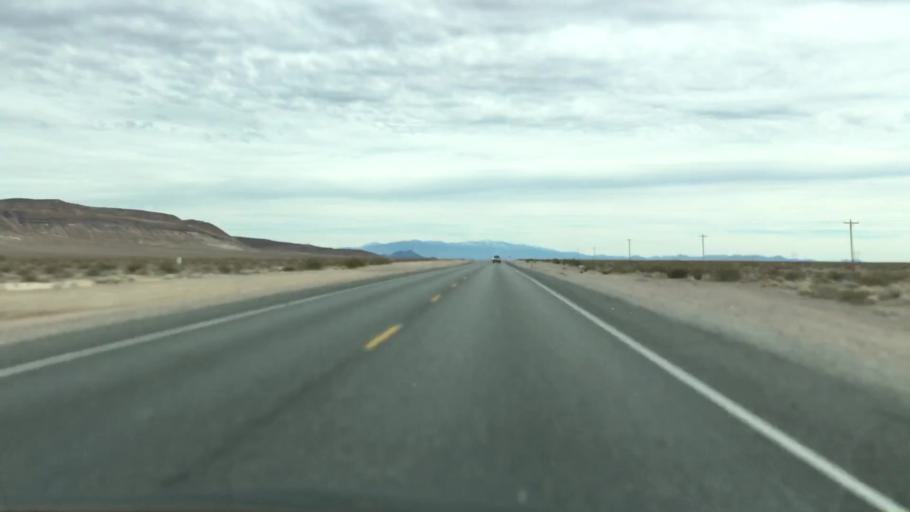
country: US
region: Nevada
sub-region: Nye County
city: Beatty
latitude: 36.6943
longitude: -116.5708
